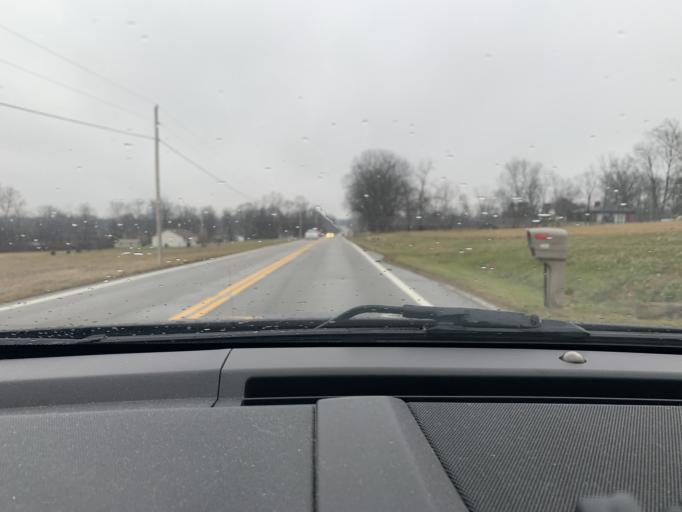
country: US
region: Ohio
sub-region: Ross County
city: Kingston
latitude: 39.4295
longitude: -82.9297
